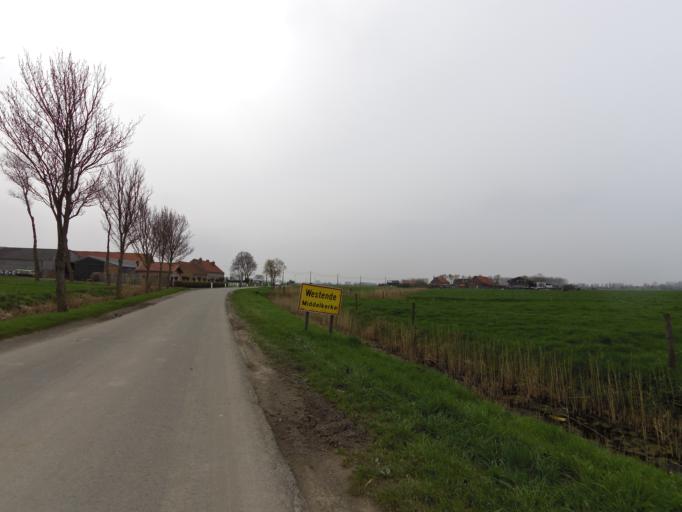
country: BE
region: Flanders
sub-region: Provincie West-Vlaanderen
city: Middelkerke
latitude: 51.1531
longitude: 2.7946
